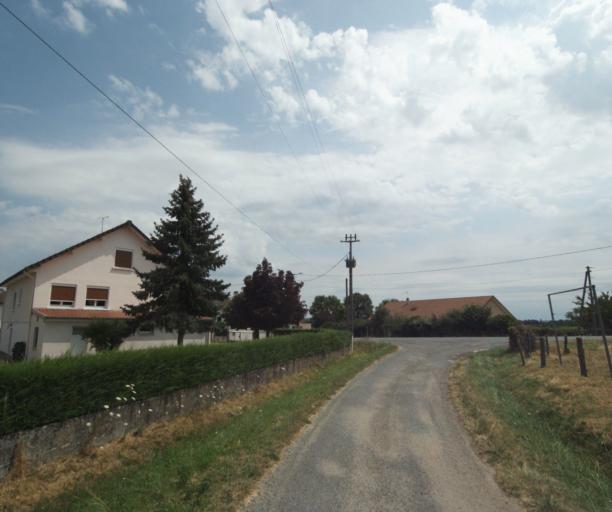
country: FR
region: Bourgogne
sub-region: Departement de Saone-et-Loire
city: Gueugnon
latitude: 46.5958
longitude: 4.0400
